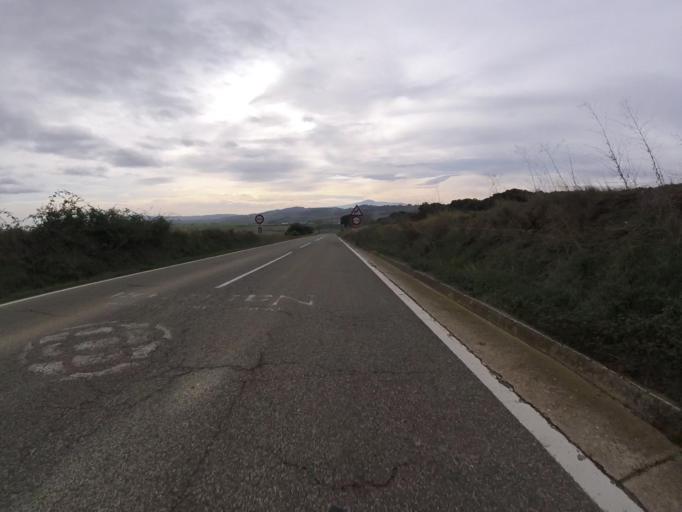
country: ES
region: Navarre
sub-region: Provincia de Navarra
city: Lezaun
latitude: 42.7307
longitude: -2.0157
